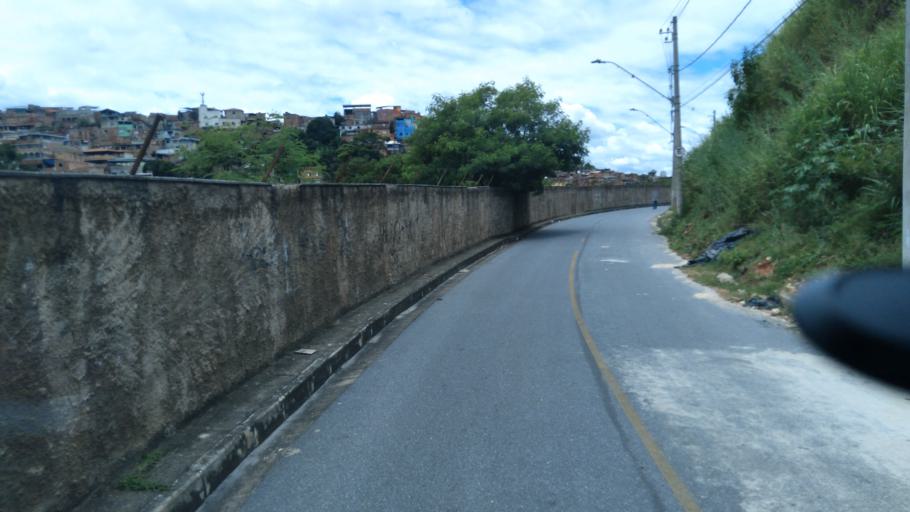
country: BR
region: Minas Gerais
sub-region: Belo Horizonte
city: Belo Horizonte
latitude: -19.9043
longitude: -43.8876
